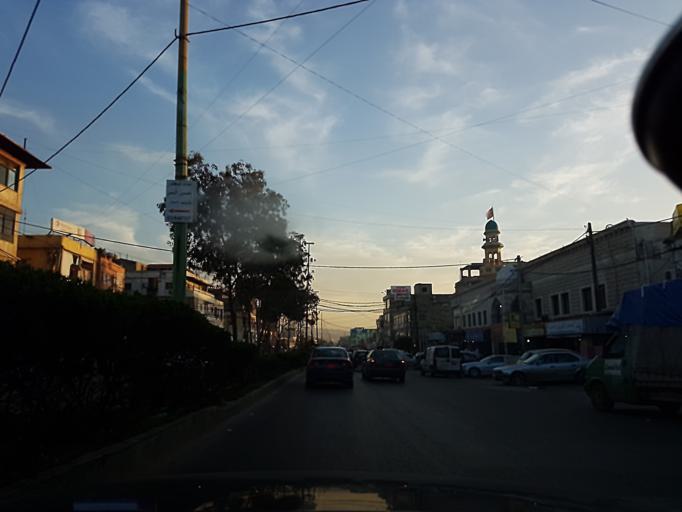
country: LB
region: Beyrouth
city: Beirut
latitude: 33.8444
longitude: 35.4849
